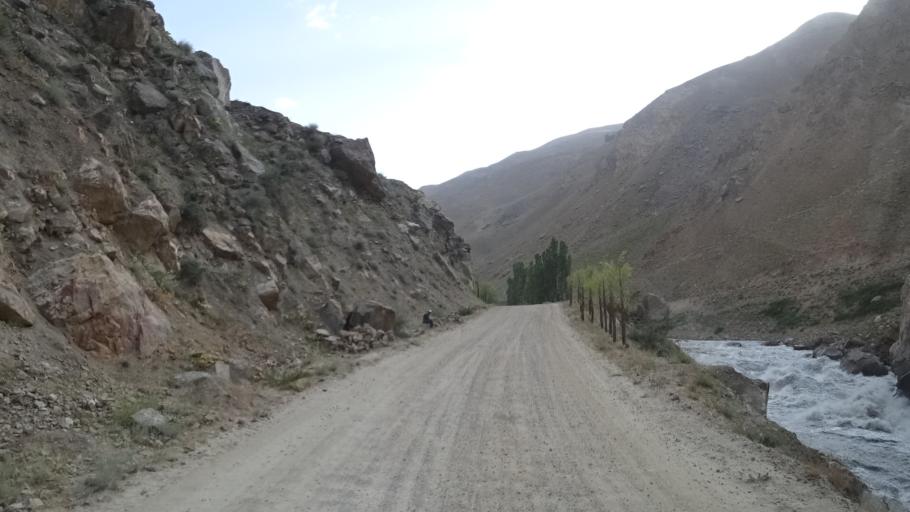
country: TJ
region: Gorno-Badakhshan
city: Khorugh
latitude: 37.2607
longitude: 71.4864
